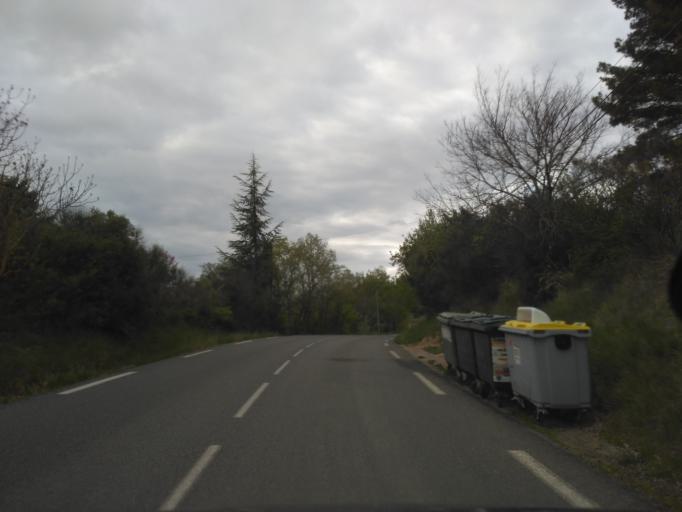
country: FR
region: Provence-Alpes-Cote d'Azur
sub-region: Departement du Var
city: Saint-Julien
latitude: 43.6289
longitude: 5.9421
